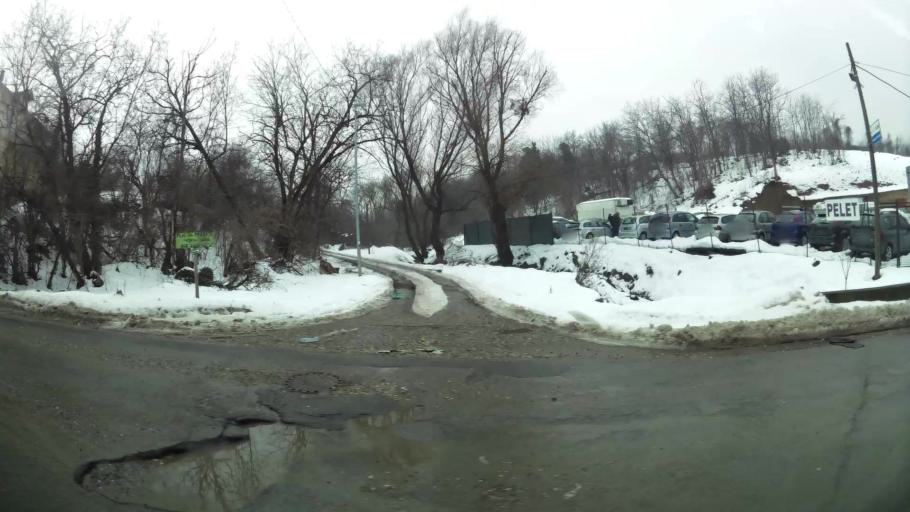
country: RS
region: Central Serbia
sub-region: Belgrade
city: Zvezdara
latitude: 44.7636
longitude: 20.5236
